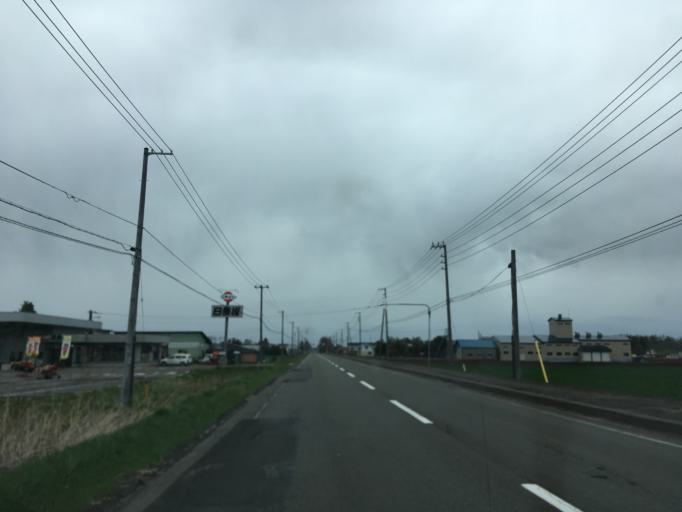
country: JP
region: Hokkaido
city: Chitose
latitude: 42.9350
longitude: 141.8059
